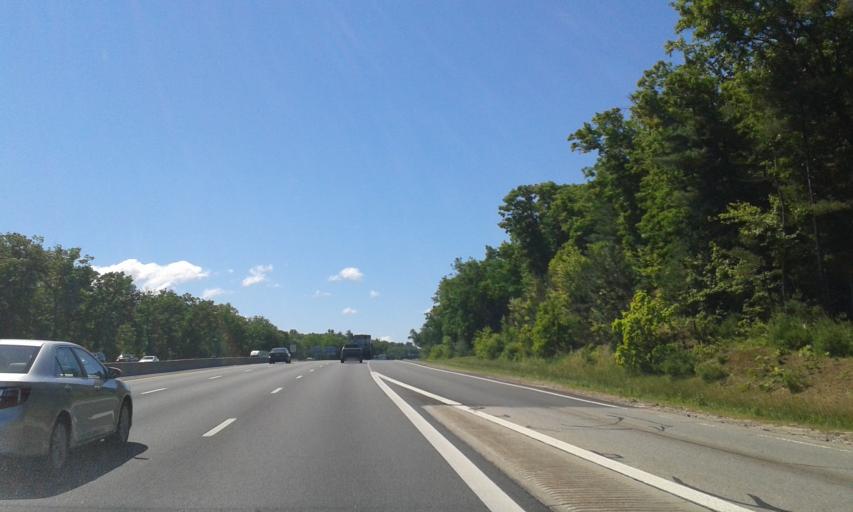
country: US
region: Massachusetts
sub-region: Middlesex County
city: Lowell
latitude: 42.5856
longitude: -71.3106
